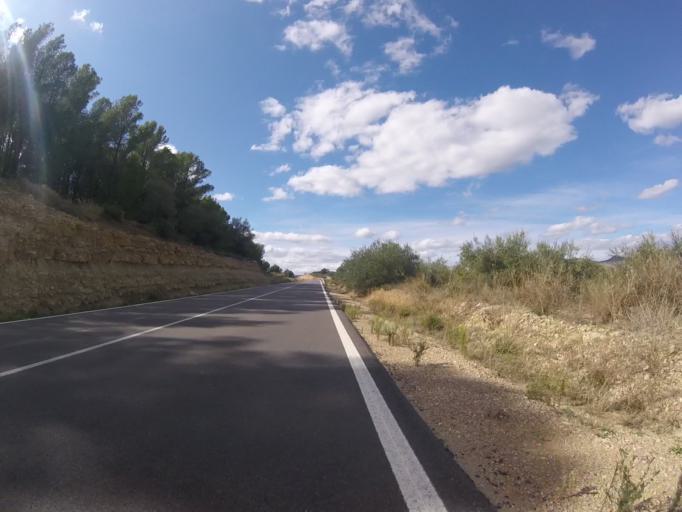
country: ES
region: Valencia
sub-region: Provincia de Castello
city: Chert/Xert
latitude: 40.4386
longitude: 0.1228
